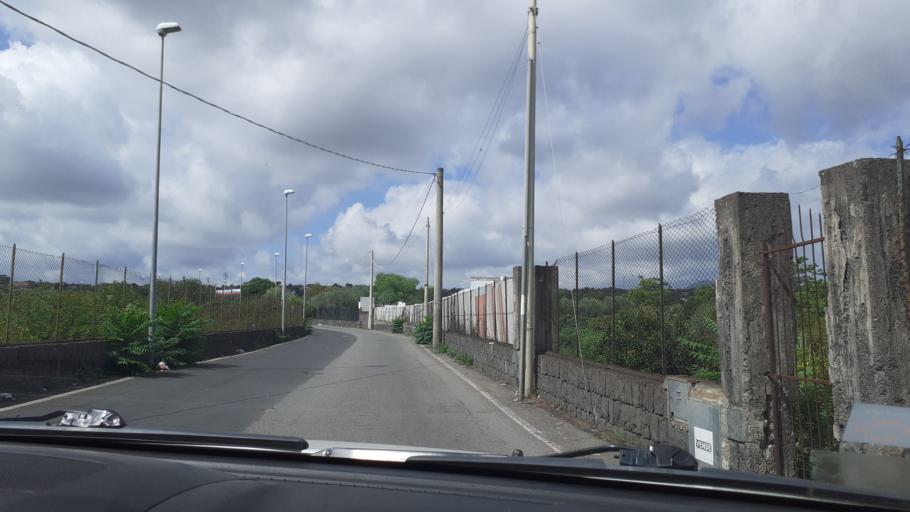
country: IT
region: Sicily
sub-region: Catania
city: San Giovanni la Punta
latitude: 37.5893
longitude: 15.0940
